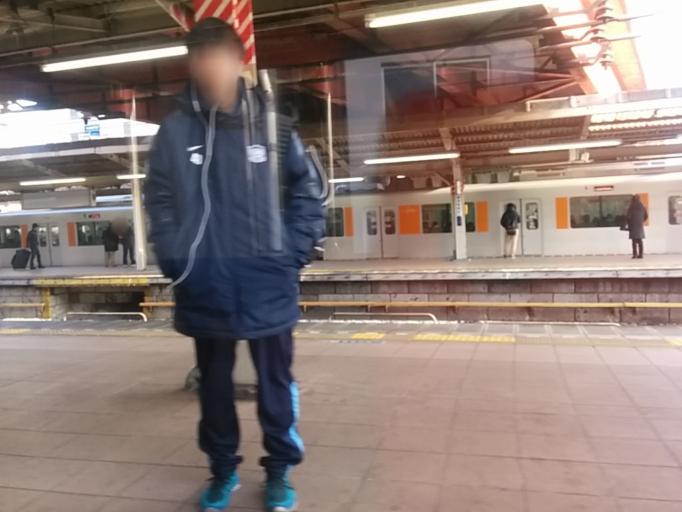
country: JP
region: Saitama
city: Asaka
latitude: 35.8141
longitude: 139.5875
